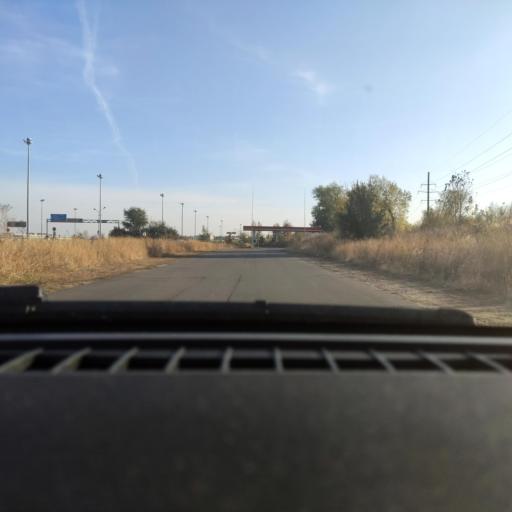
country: RU
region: Voronezj
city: Somovo
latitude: 51.6582
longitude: 39.3015
